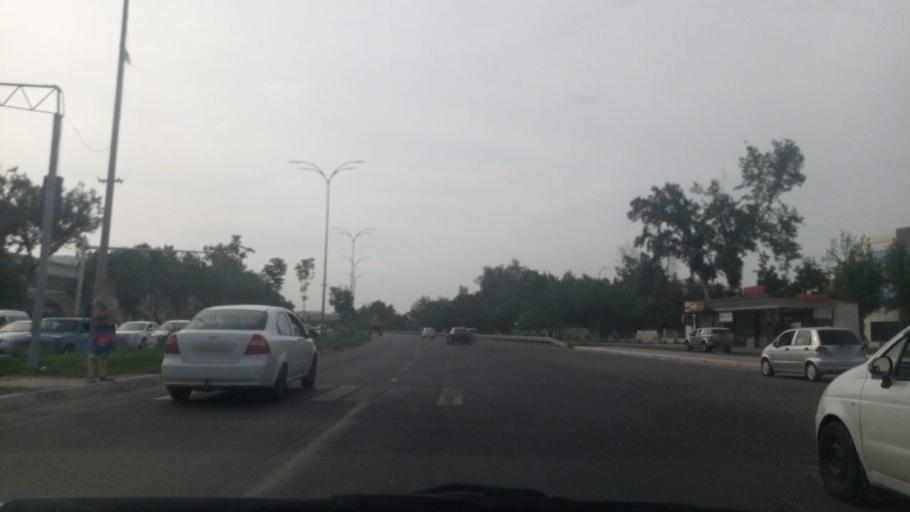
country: UZ
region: Toshkent
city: Salor
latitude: 41.2961
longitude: 69.3531
